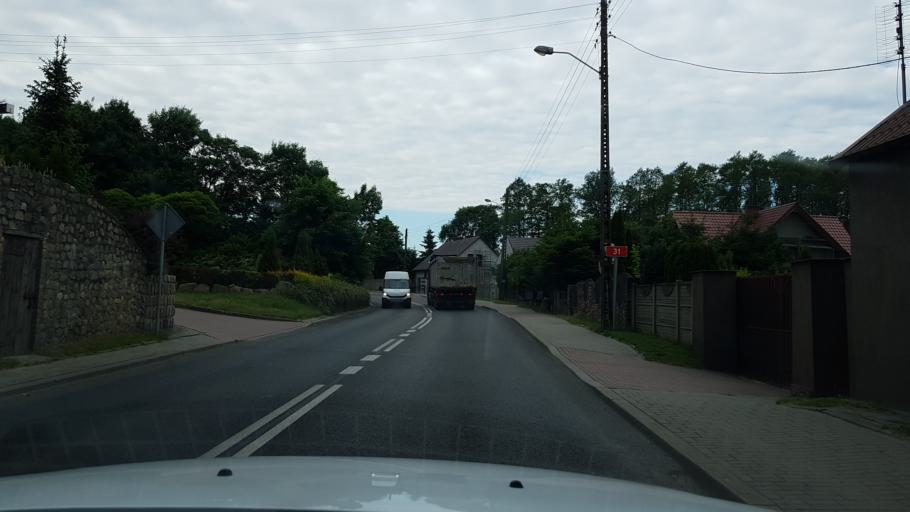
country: PL
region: West Pomeranian Voivodeship
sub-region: Powiat gryfinski
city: Gryfino
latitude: 53.2851
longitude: 14.5156
